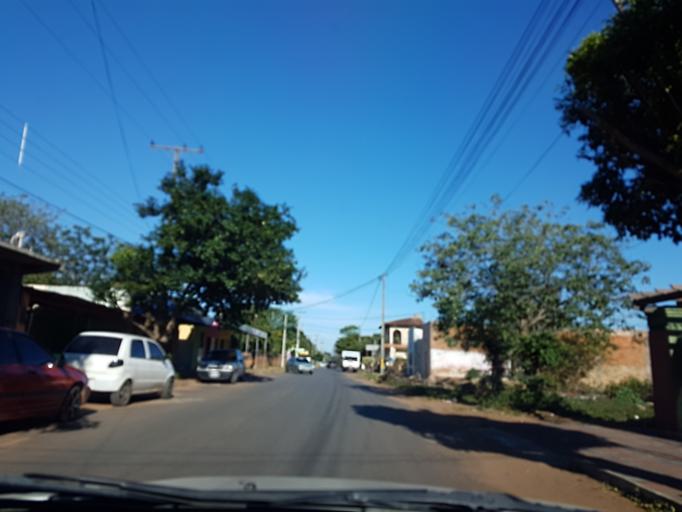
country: PY
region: Central
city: San Lorenzo
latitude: -25.2757
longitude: -57.4687
